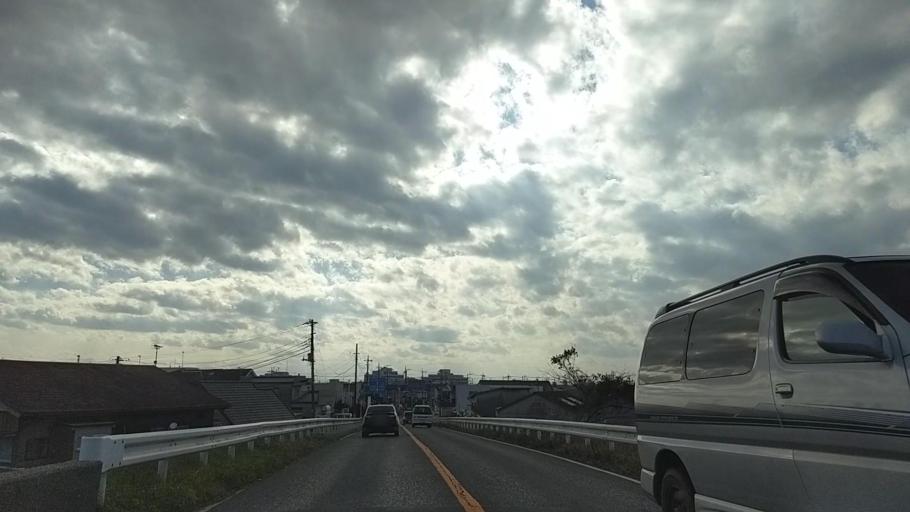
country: JP
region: Chiba
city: Naruto
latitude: 35.6084
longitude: 140.4145
